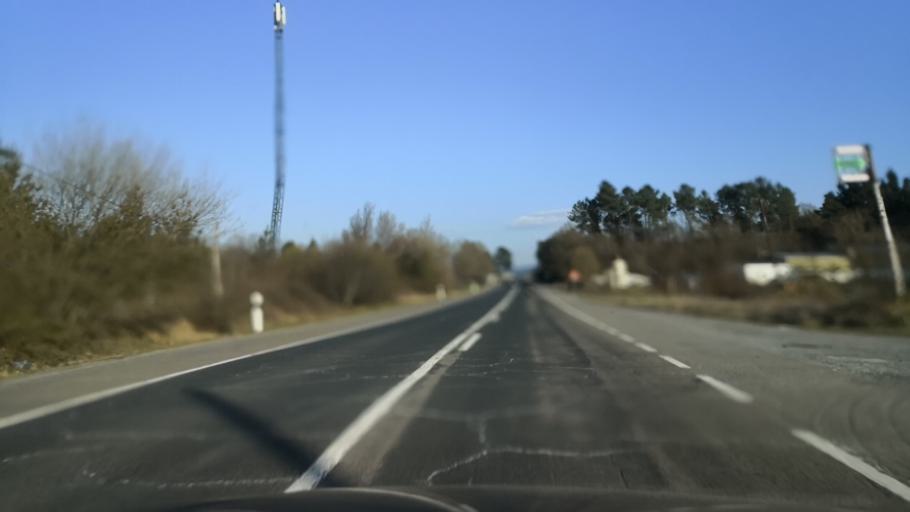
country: ES
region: Galicia
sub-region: Provincia de Lugo
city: Corgo
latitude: 42.9373
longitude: -7.4122
